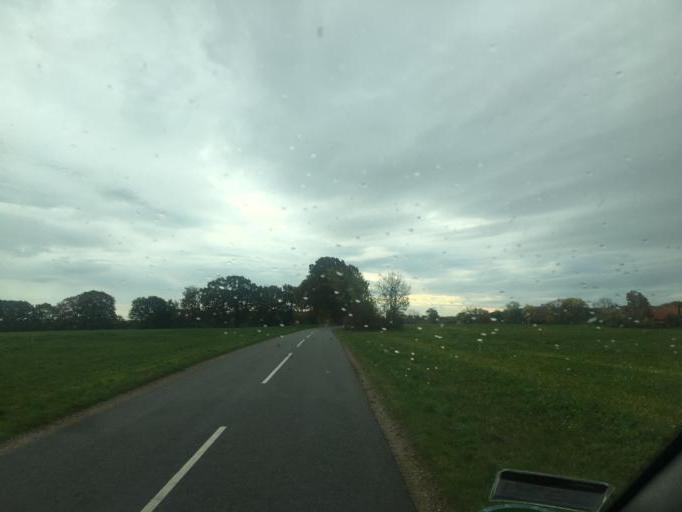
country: DK
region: Zealand
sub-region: Koge Kommune
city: Bjaeverskov
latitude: 55.4133
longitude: 11.9832
